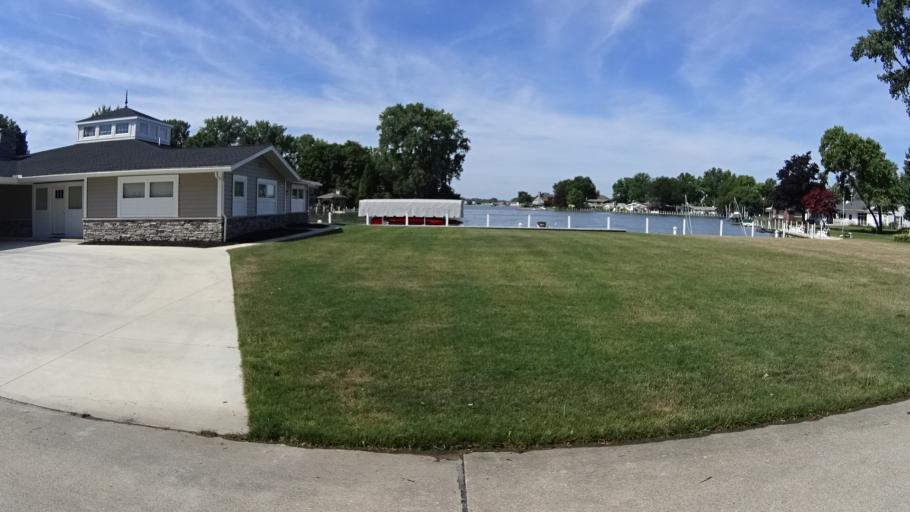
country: US
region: Ohio
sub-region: Erie County
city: Sandusky
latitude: 41.4625
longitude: -82.6615
